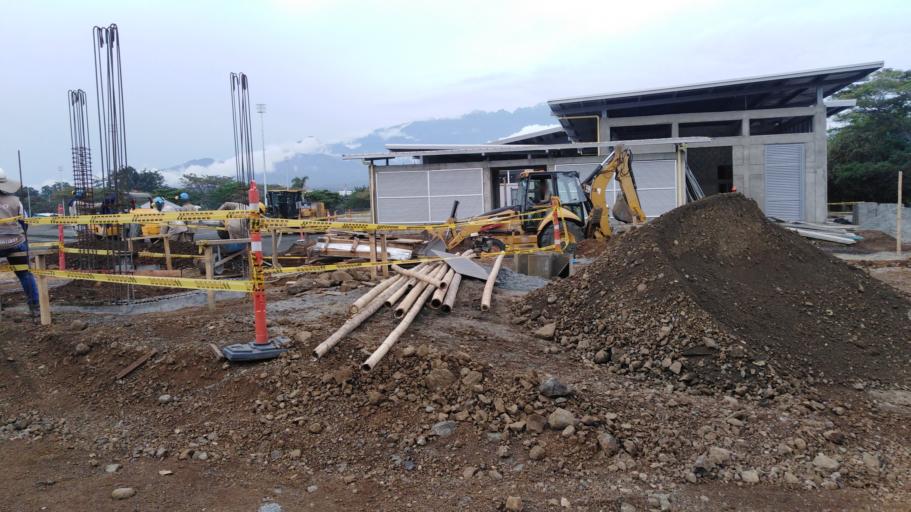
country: CO
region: Valle del Cauca
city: Cali
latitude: 3.3610
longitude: -76.5207
